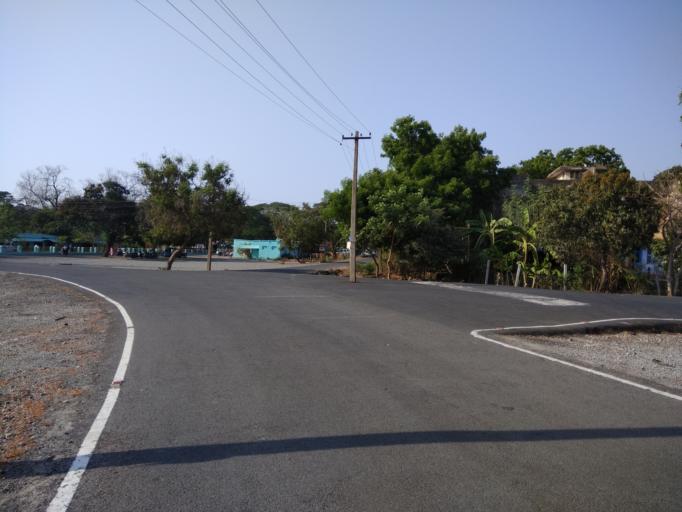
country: IN
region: Tamil Nadu
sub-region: Kancheepuram
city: Saint Thomas Mount
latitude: 13.0150
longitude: 80.1891
